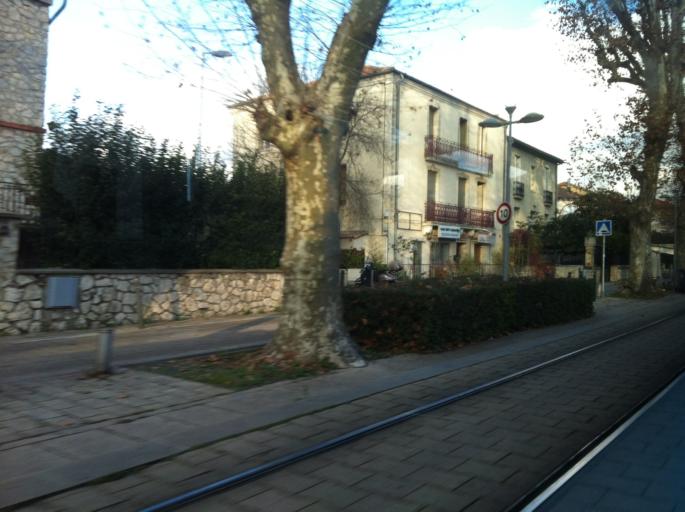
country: FR
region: Languedoc-Roussillon
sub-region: Departement de l'Herault
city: Montpellier
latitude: 43.6233
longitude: 3.8677
